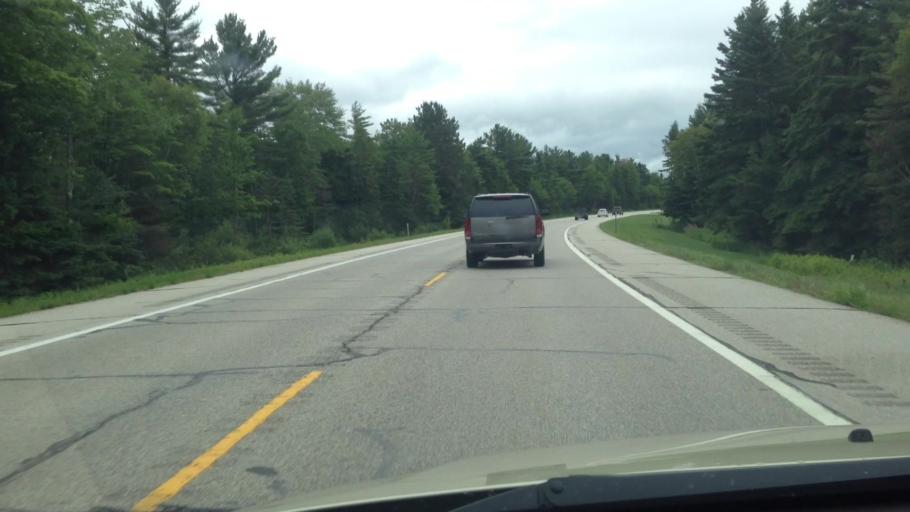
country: US
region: Michigan
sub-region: Luce County
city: Newberry
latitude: 46.1043
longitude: -85.4264
